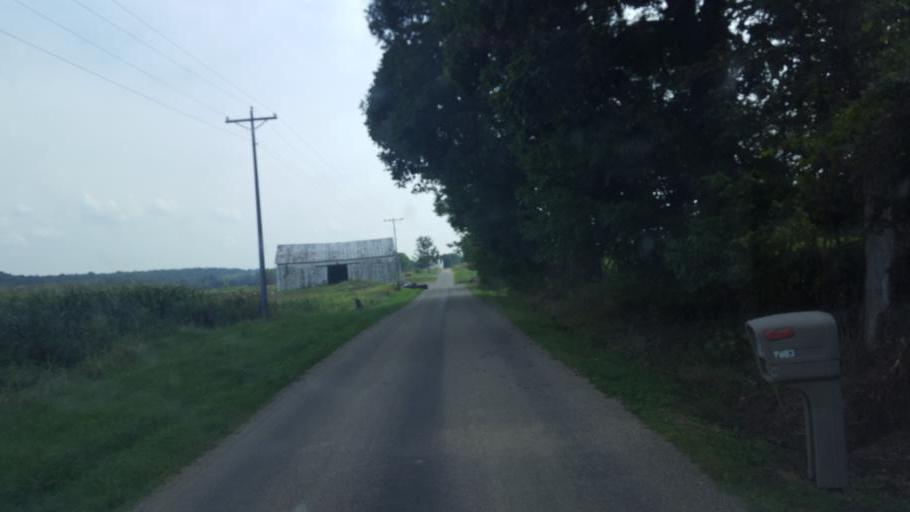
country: US
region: Ohio
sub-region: Knox County
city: Gambier
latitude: 40.3411
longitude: -82.3878
